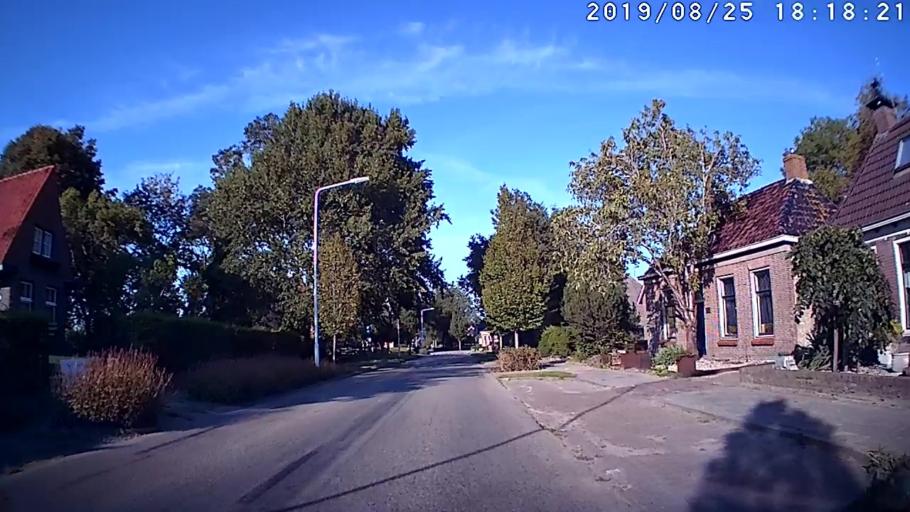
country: NL
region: Friesland
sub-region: Gemeente Gaasterlan-Sleat
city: Balk
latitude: 52.8706
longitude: 5.5976
